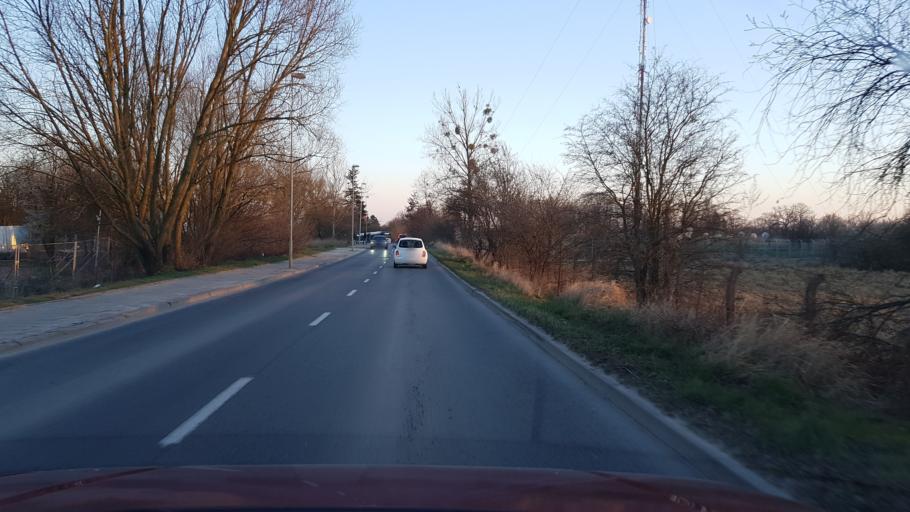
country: PL
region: West Pomeranian Voivodeship
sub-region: Szczecin
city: Szczecin
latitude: 53.4771
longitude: 14.5446
